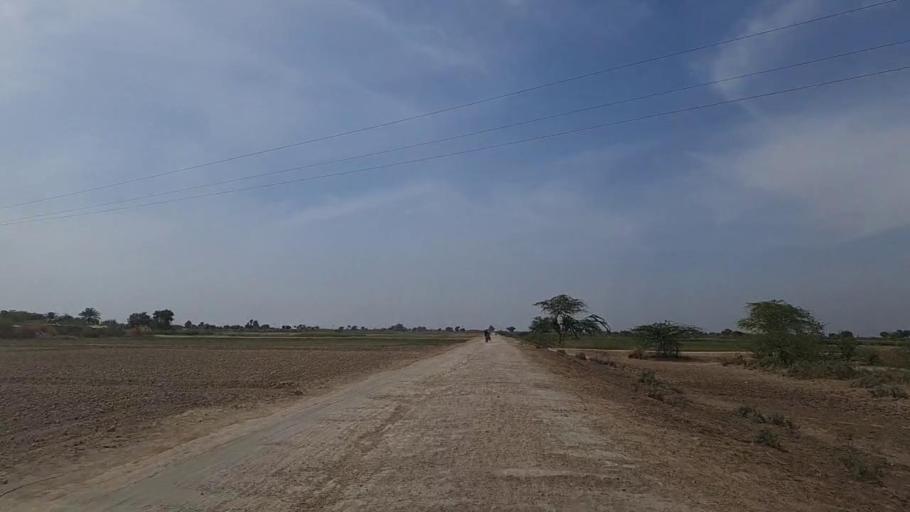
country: PK
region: Sindh
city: Kunri
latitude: 25.2127
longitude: 69.4960
